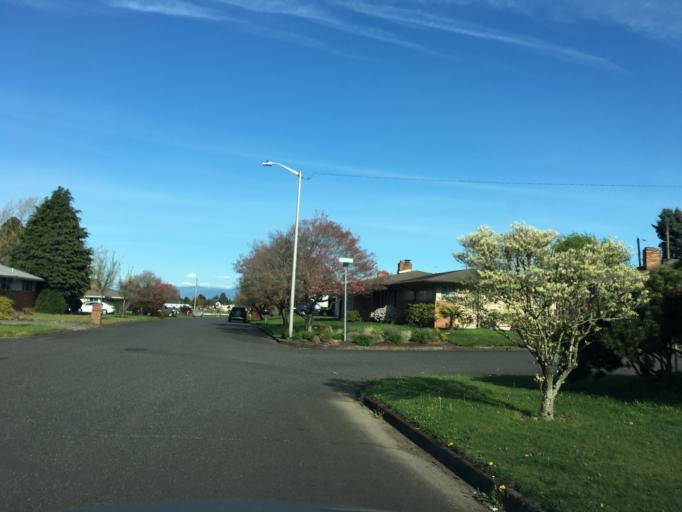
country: US
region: Oregon
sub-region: Multnomah County
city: Lents
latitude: 45.5494
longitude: -122.5349
